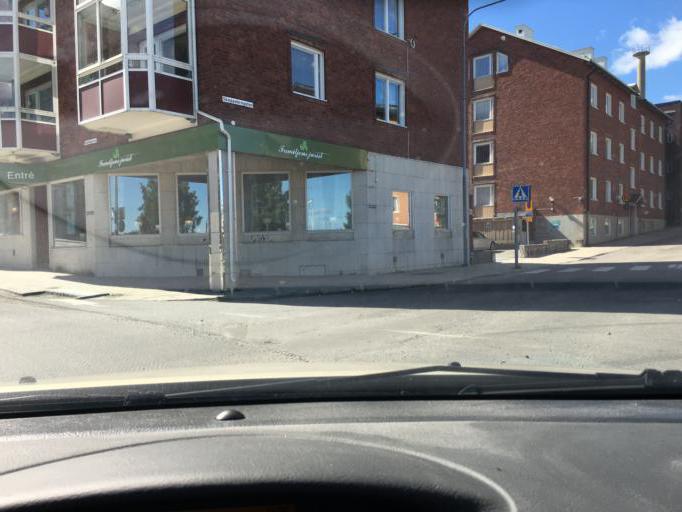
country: SE
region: Norrbotten
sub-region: Lulea Kommun
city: Lulea
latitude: 65.5843
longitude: 22.1439
